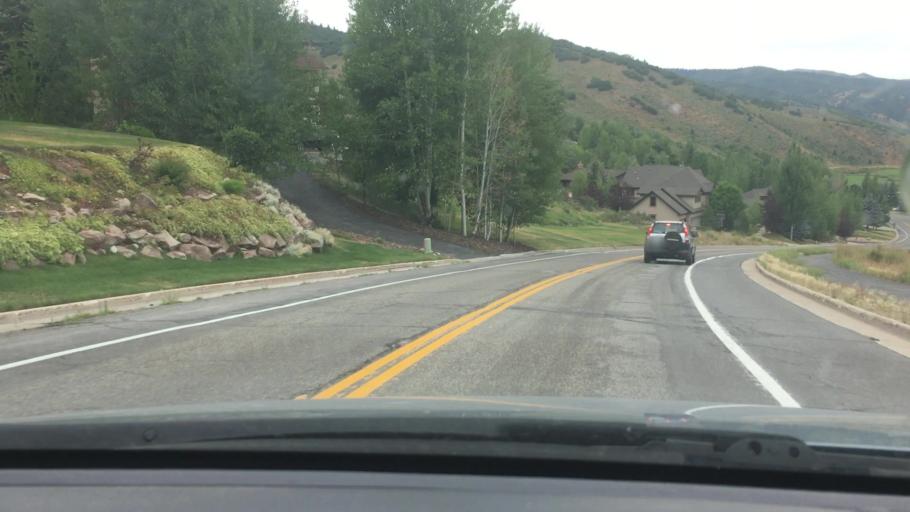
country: US
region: Utah
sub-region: Summit County
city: Summit Park
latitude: 40.7606
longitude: -111.5777
